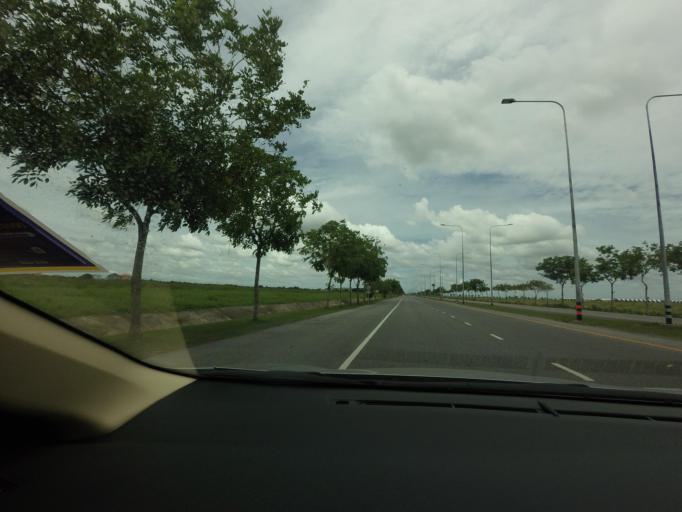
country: TH
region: Bangkok
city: Lat Krabang
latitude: 13.7063
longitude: 100.7743
